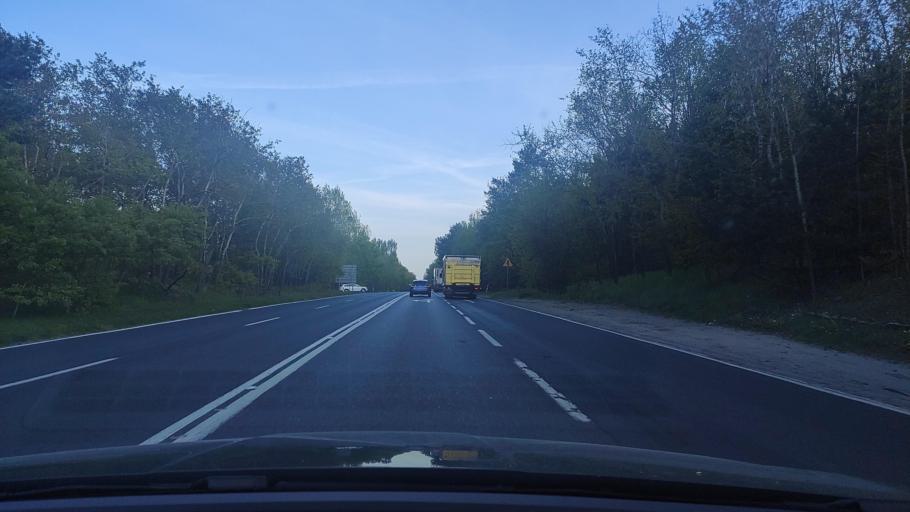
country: PL
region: Greater Poland Voivodeship
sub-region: Powiat poznanski
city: Czerwonak
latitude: 52.4274
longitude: 17.0123
